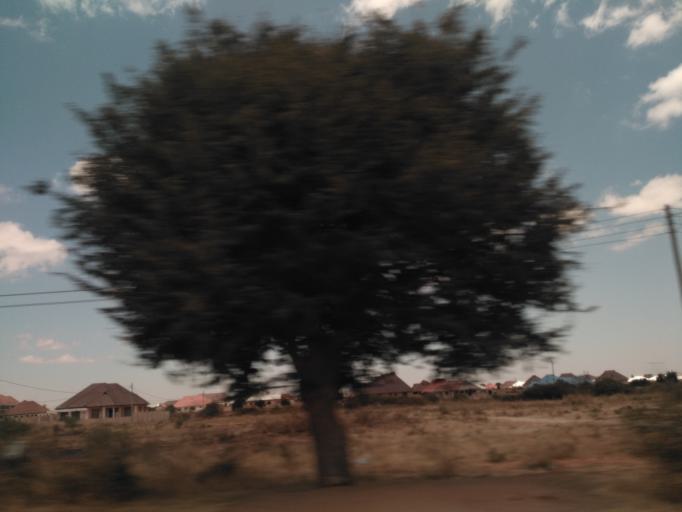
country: TZ
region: Dodoma
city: Kisasa
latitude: -6.1801
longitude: 35.7935
